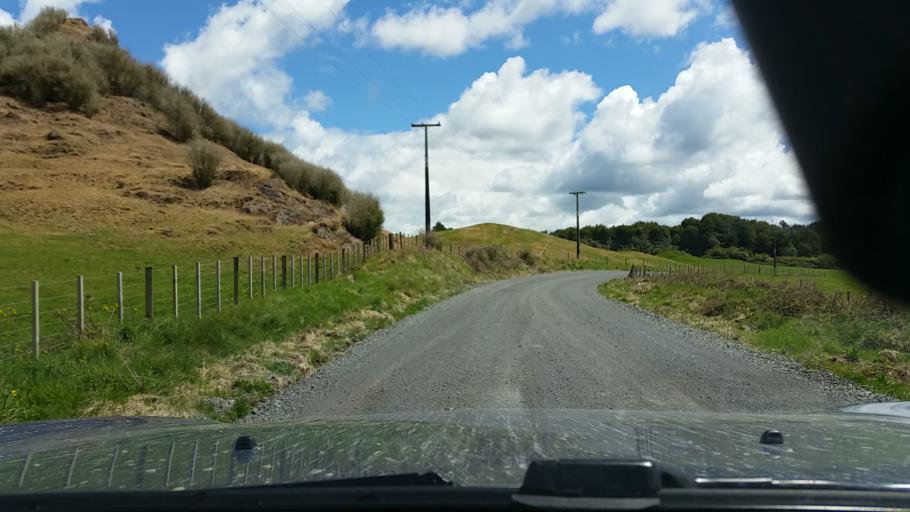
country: NZ
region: Bay of Plenty
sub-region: Rotorua District
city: Rotorua
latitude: -38.0828
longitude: 176.0555
